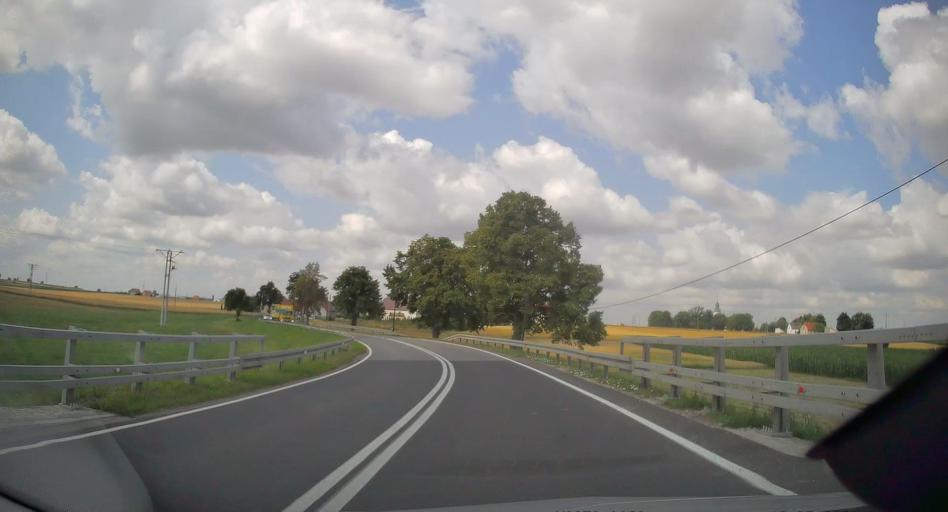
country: PL
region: Opole Voivodeship
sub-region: Powiat kedzierzynsko-kozielski
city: Wiekszyce
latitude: 50.3339
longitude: 18.0733
